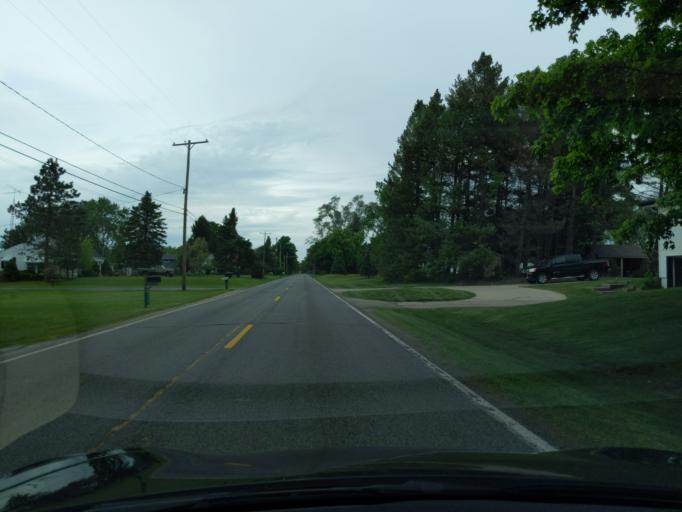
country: US
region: Michigan
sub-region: Ingham County
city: Leslie
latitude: 42.3766
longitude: -84.3492
